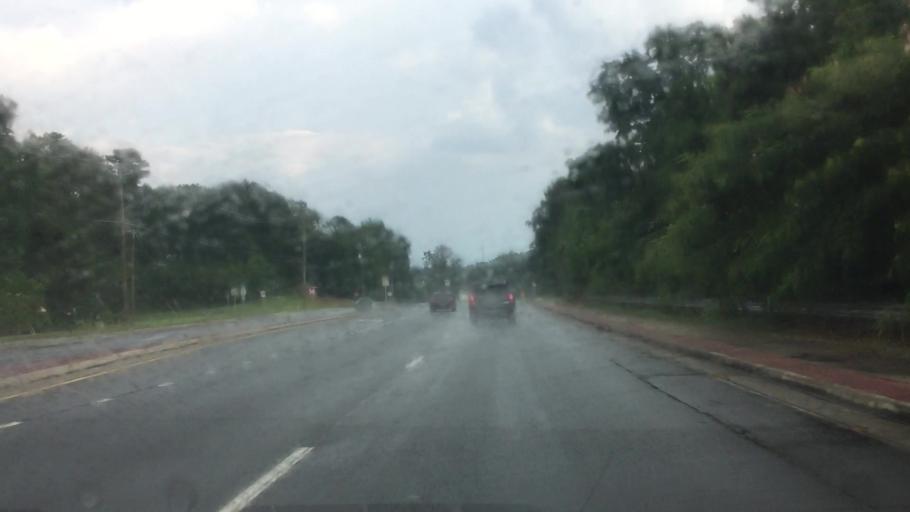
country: US
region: Georgia
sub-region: DeKalb County
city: Panthersville
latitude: 33.6945
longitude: -84.2046
